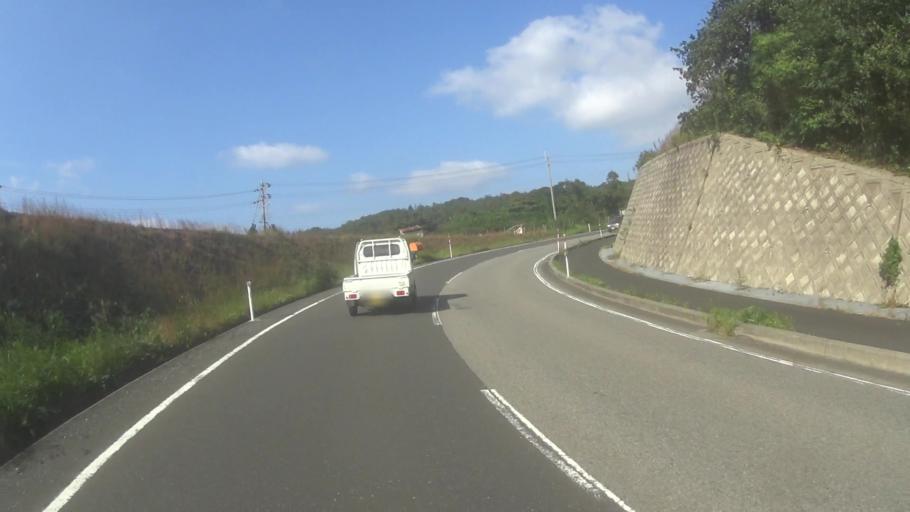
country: JP
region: Kyoto
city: Miyazu
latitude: 35.6930
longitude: 135.0496
